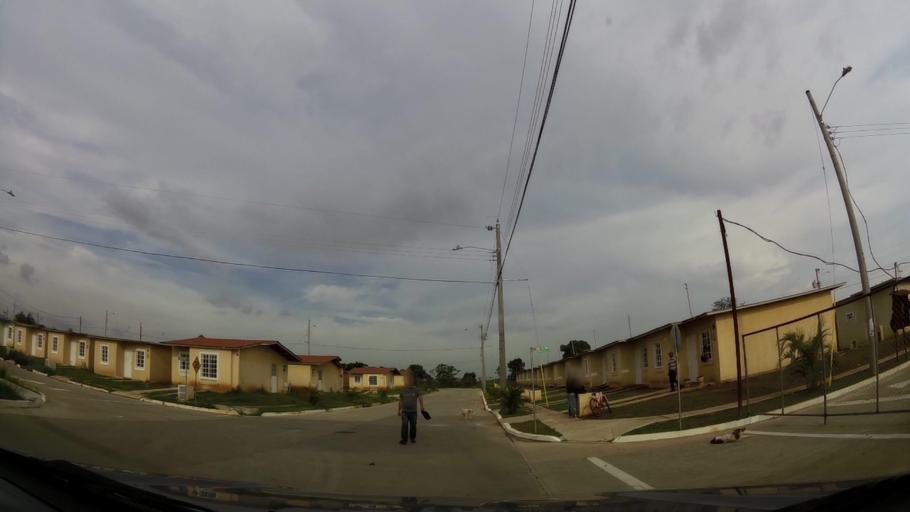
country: PA
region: Panama
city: Tocumen
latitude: 9.0774
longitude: -79.3525
